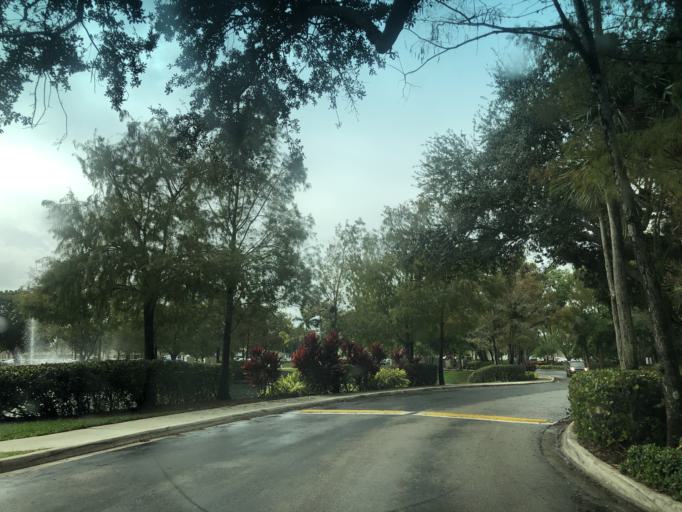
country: US
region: Florida
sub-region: Broward County
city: Tamarac
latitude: 26.2444
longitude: -80.2477
